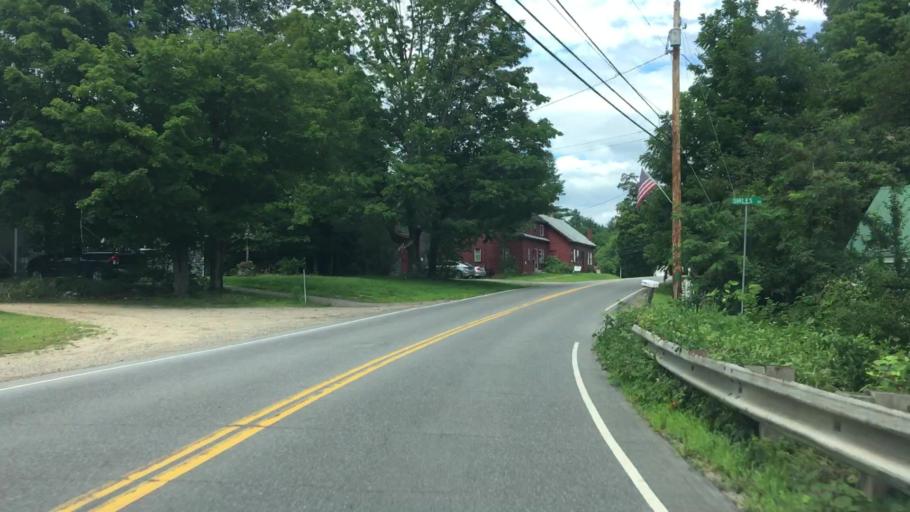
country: US
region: New Hampshire
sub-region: Belknap County
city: Meredith
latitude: 43.6140
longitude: -71.5333
